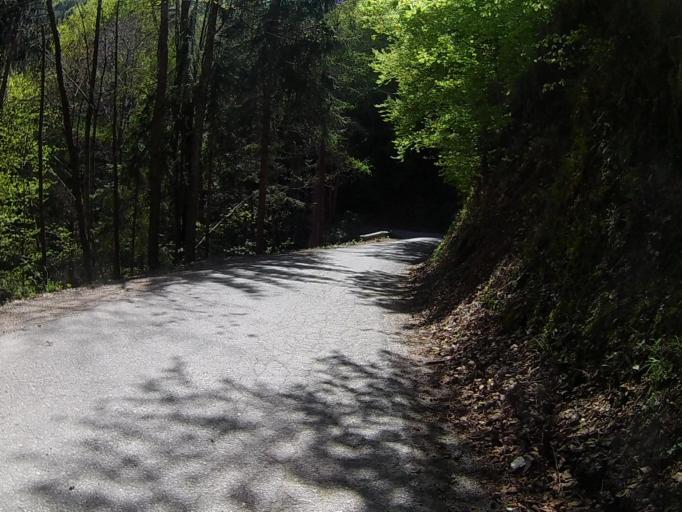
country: SI
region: Ruse
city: Ruse
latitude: 46.5235
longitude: 15.5153
